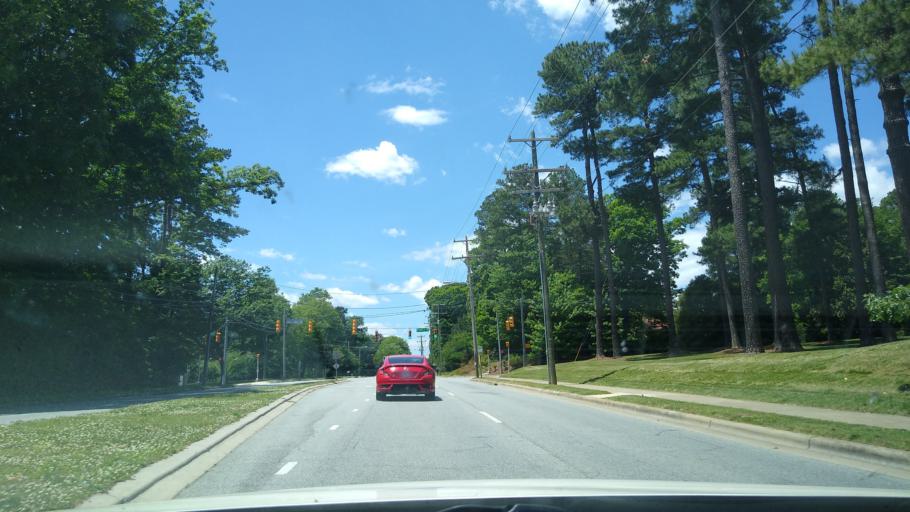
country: US
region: North Carolina
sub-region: Guilford County
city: Greensboro
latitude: 36.0908
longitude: -79.8577
